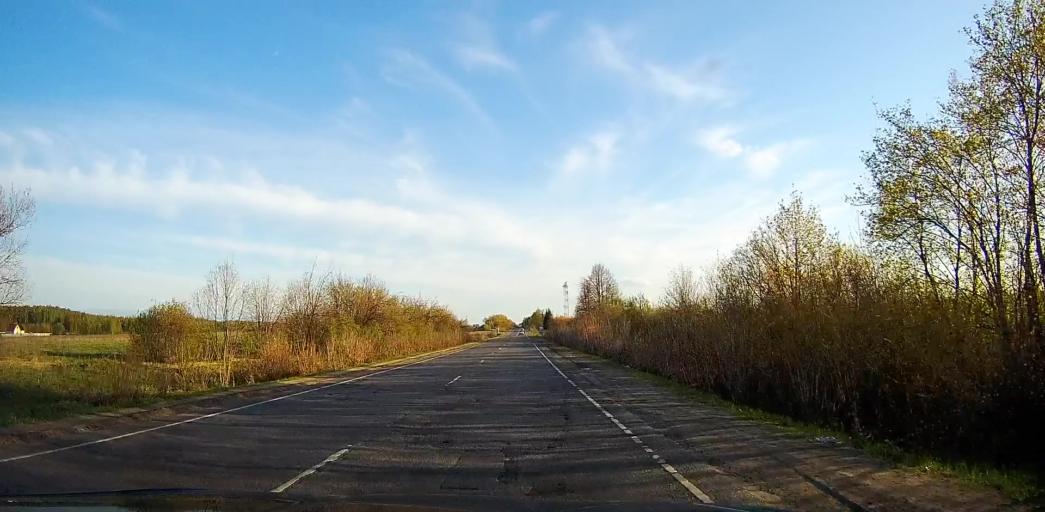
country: RU
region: Moskovskaya
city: Bronnitsy
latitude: 55.3222
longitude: 38.2186
